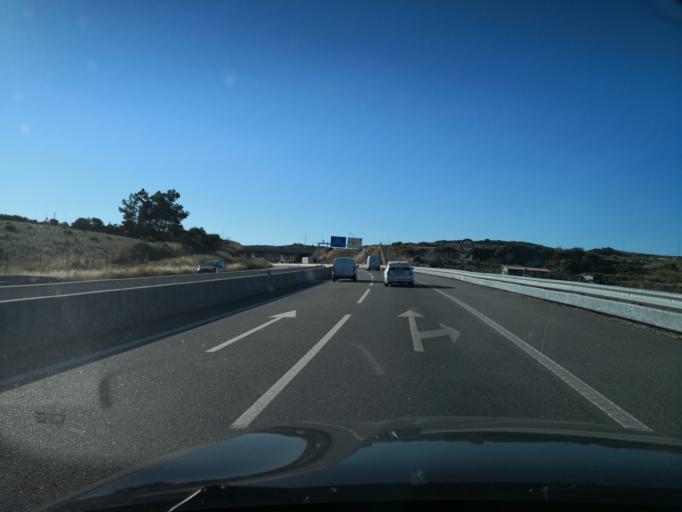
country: PT
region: Vila Real
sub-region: Murca
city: Murca
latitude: 41.3825
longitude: -7.5072
